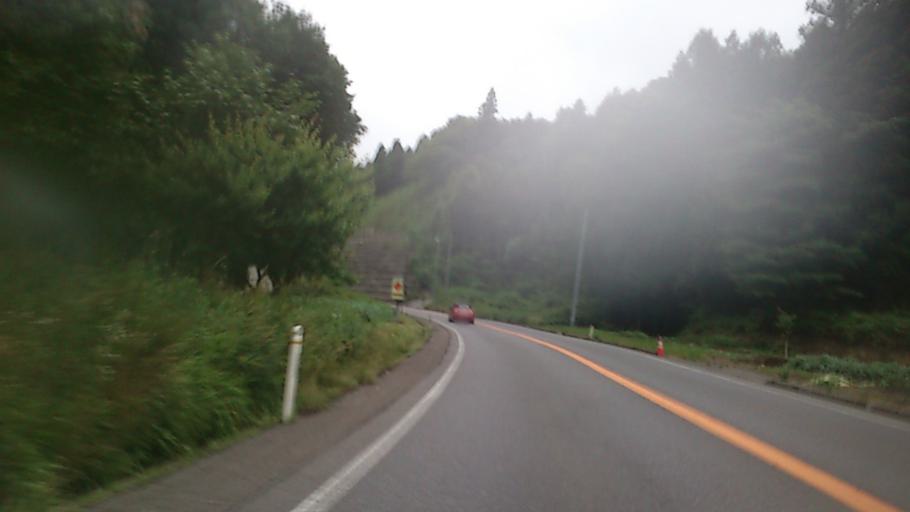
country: JP
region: Fukushima
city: Sukagawa
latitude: 37.1550
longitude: 140.2513
